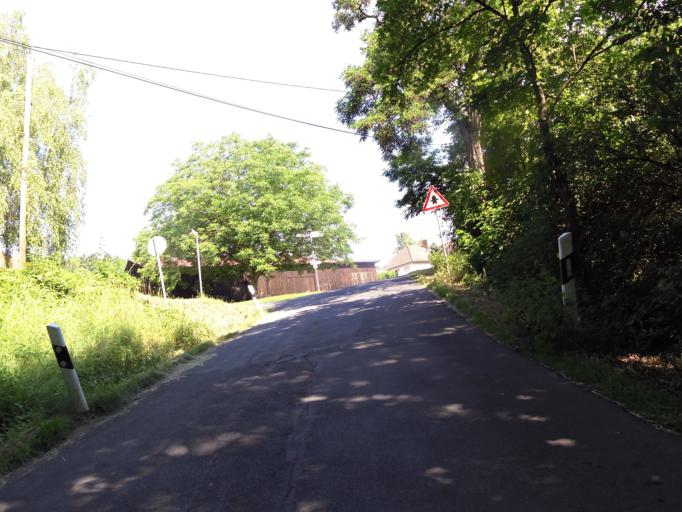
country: DE
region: Bavaria
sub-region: Regierungsbezirk Unterfranken
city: Hochberg
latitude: 49.7768
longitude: 9.9153
